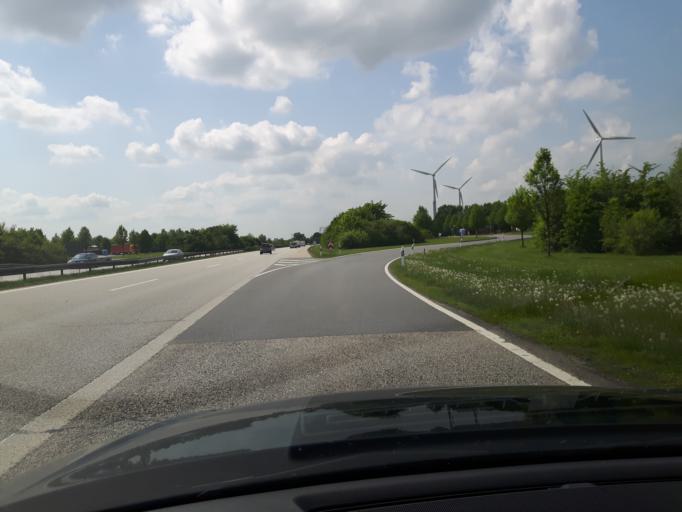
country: DE
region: Mecklenburg-Vorpommern
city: Muhlen Eichsen
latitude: 53.8273
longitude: 11.2556
